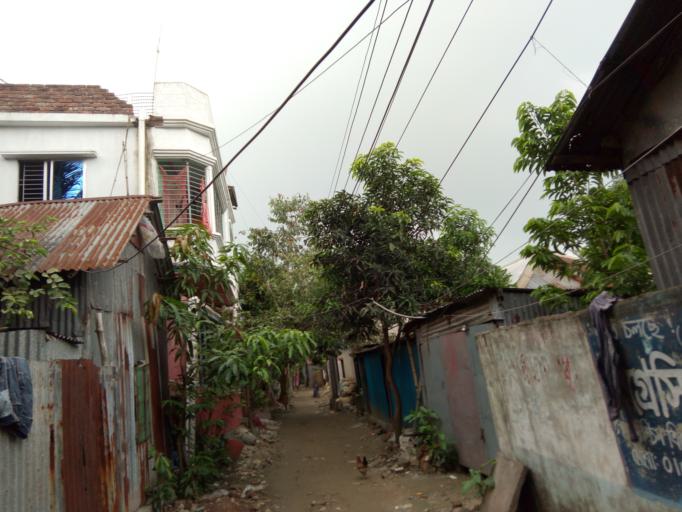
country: BD
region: Dhaka
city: Paltan
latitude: 23.7590
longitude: 90.4537
